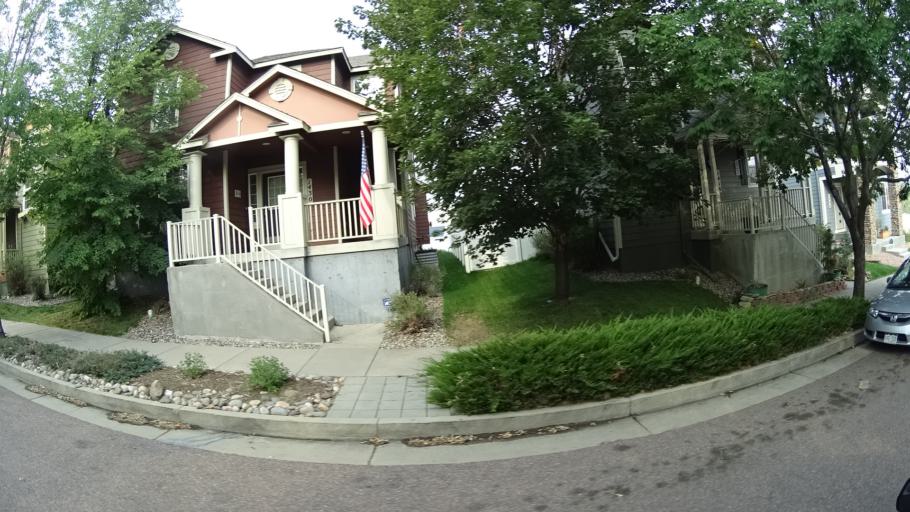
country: US
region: Colorado
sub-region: El Paso County
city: Stratmoor
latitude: 38.8112
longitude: -104.7866
